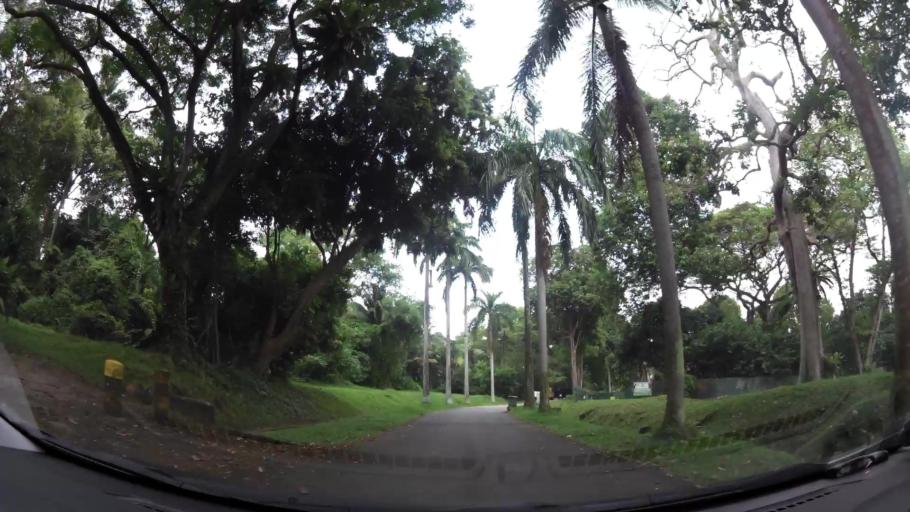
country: SG
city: Singapore
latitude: 1.2849
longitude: 103.7975
